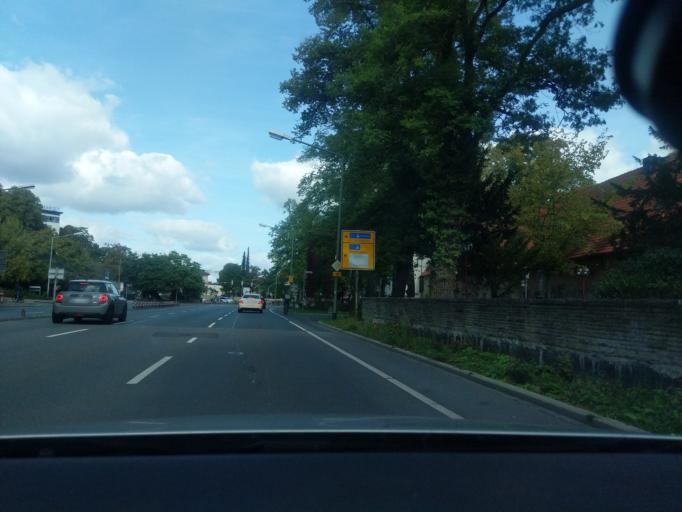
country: DE
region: Lower Saxony
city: Osnabrueck
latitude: 52.2774
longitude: 8.0383
